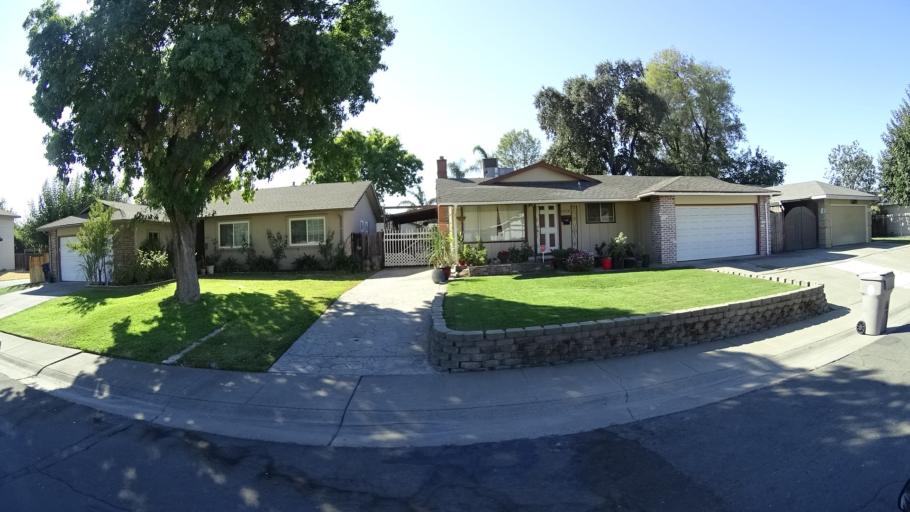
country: US
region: California
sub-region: Sacramento County
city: Florin
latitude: 38.4666
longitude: -121.4289
